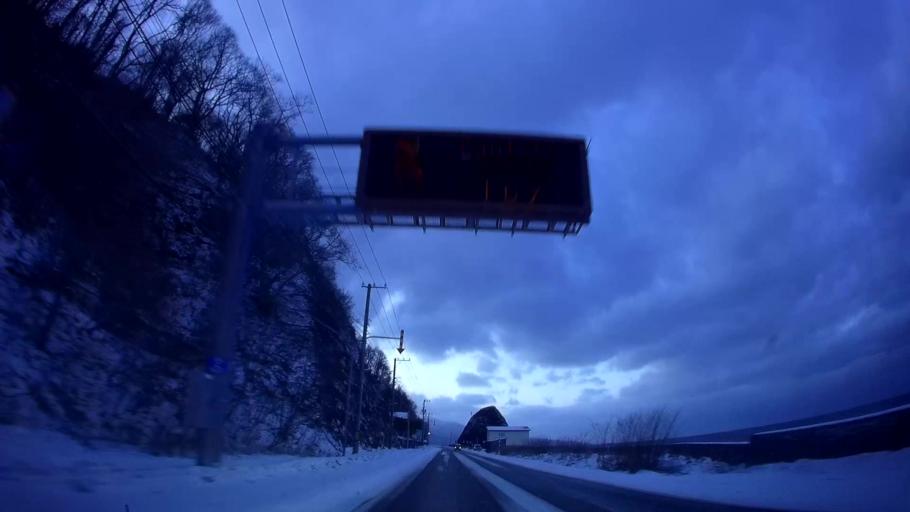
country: JP
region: Hokkaido
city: Hakodate
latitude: 41.8922
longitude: 141.0486
